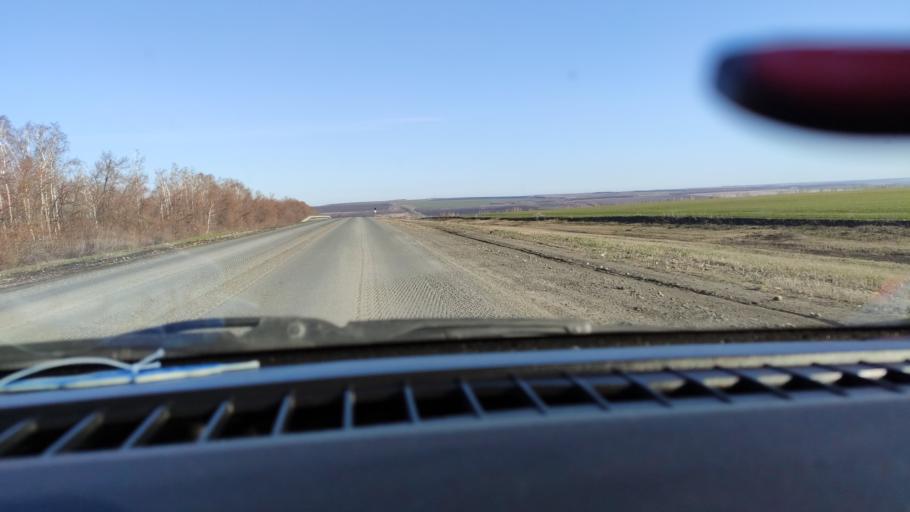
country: RU
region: Saratov
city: Dukhovnitskoye
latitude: 52.7211
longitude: 48.2645
